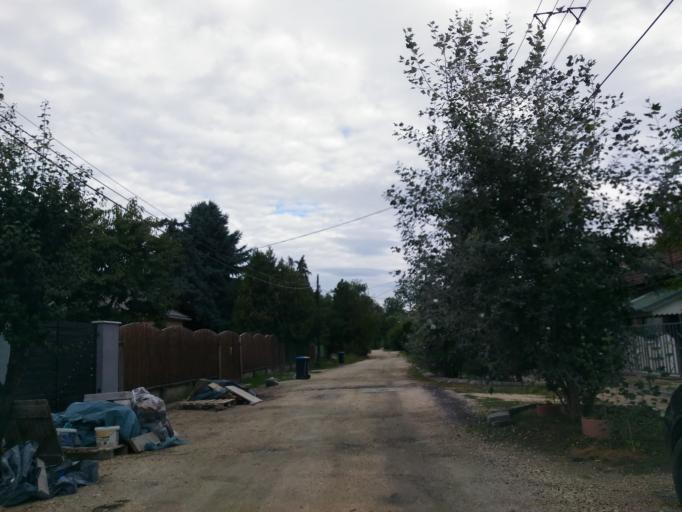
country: HU
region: Pest
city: Halasztelek
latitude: 47.3909
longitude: 18.9761
